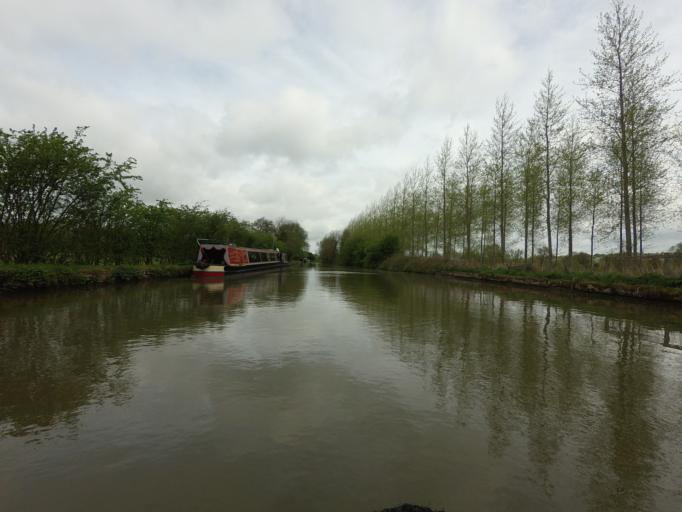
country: GB
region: England
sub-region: Milton Keynes
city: Water Eaton
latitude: 51.9534
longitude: -0.7070
